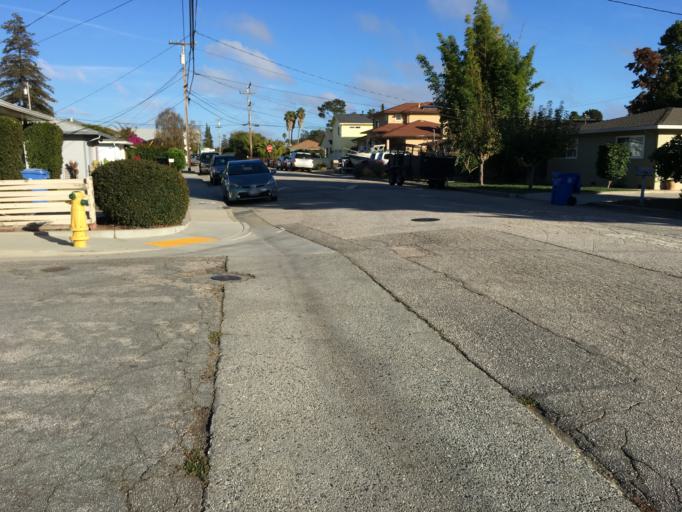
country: US
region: California
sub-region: Santa Cruz County
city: Twin Lakes
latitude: 36.9894
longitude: -122.0058
